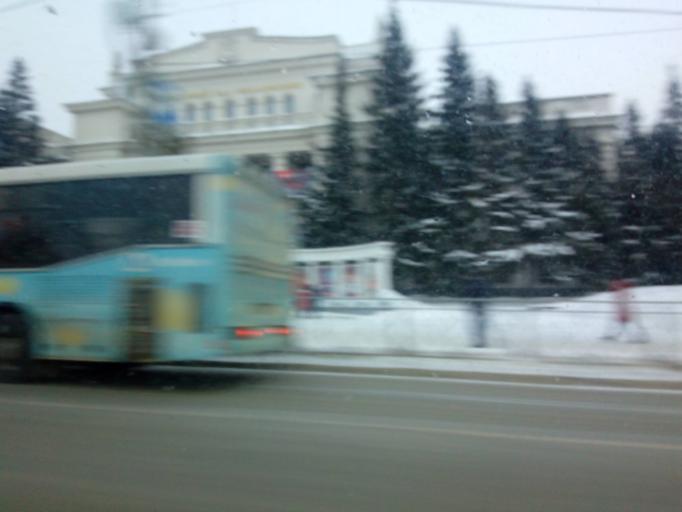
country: RU
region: Novosibirsk
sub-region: Novosibirskiy Rayon
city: Novosibirsk
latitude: 55.0277
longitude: 82.9212
